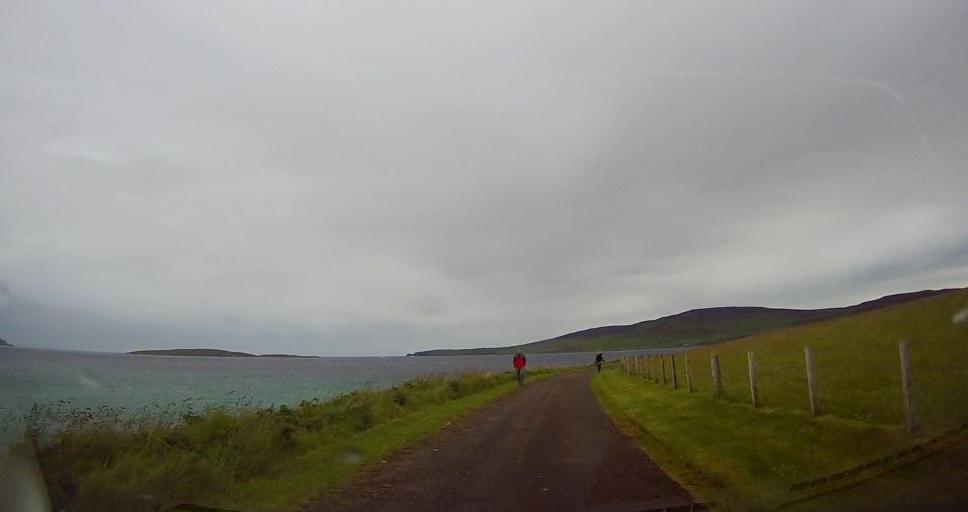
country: GB
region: Scotland
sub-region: Orkney Islands
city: Orkney
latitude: 59.1219
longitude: -3.0852
